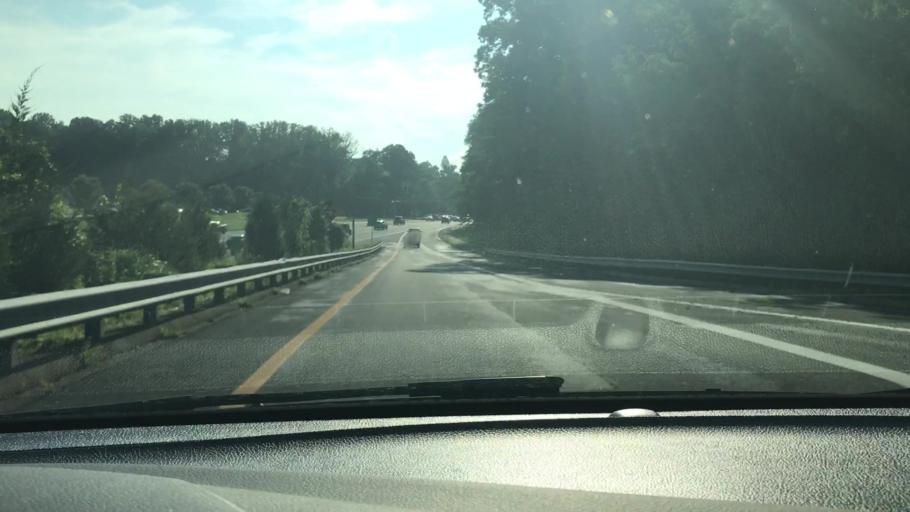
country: US
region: Virginia
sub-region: Fairfax County
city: Merrifield
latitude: 38.8655
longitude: -77.2113
